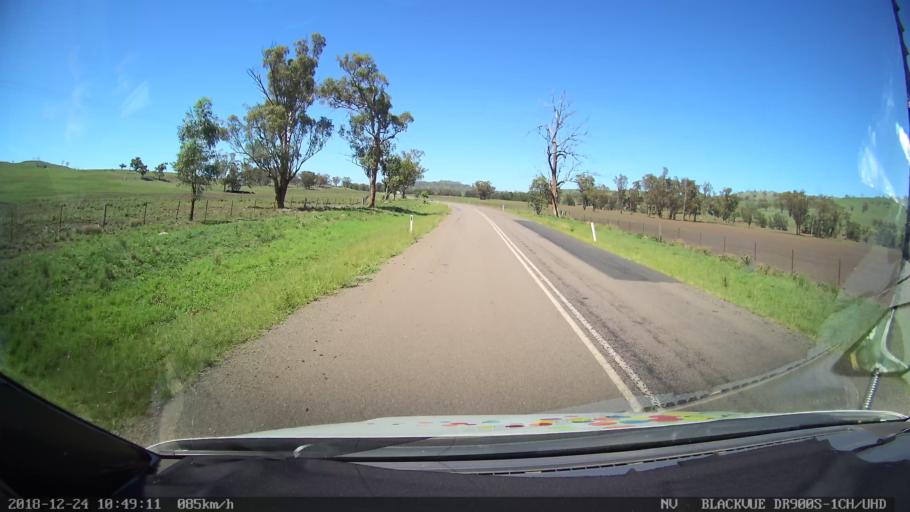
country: AU
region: New South Wales
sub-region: Upper Hunter Shire
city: Merriwa
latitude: -31.9444
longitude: 150.4287
